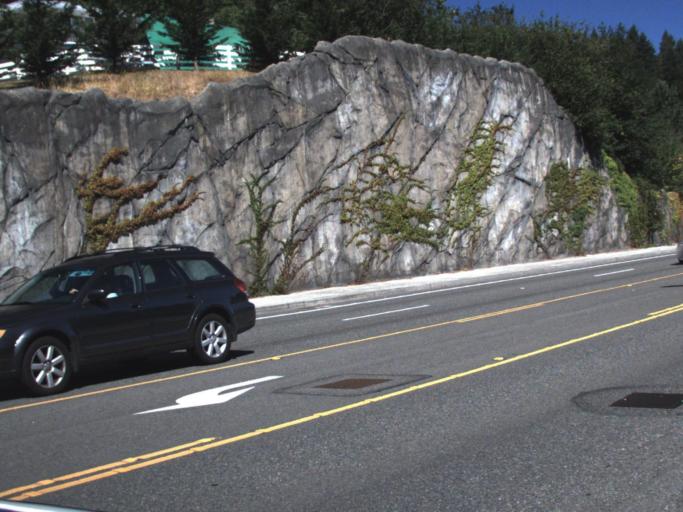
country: US
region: Washington
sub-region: King County
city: Issaquah
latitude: 47.5338
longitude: -122.0623
